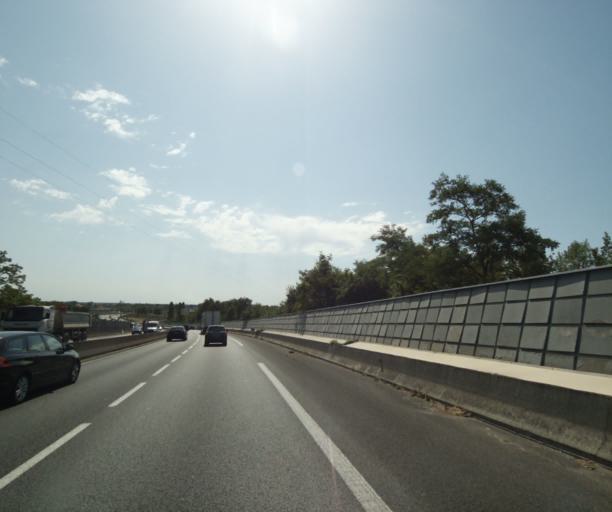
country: FR
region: Midi-Pyrenees
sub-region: Departement du Tarn-et-Garonne
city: Montauban
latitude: 43.9971
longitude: 1.3559
